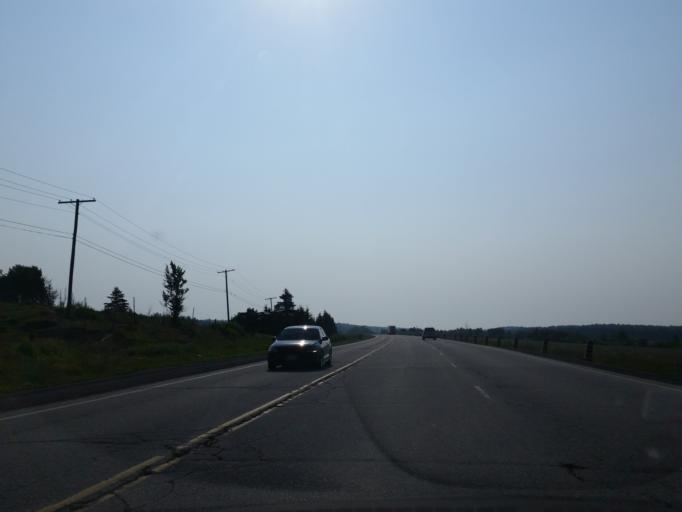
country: CA
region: Ontario
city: Greater Sudbury
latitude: 46.4307
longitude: -80.2472
